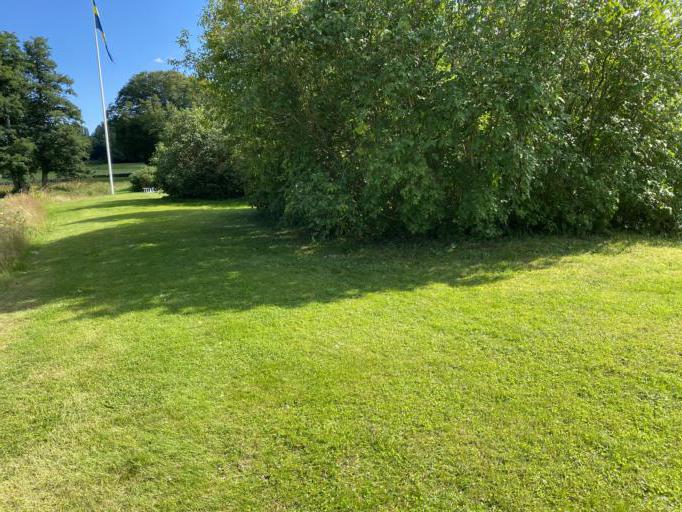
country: SE
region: Skane
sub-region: Hassleholms Kommun
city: Tormestorp
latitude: 56.1054
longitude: 13.7131
